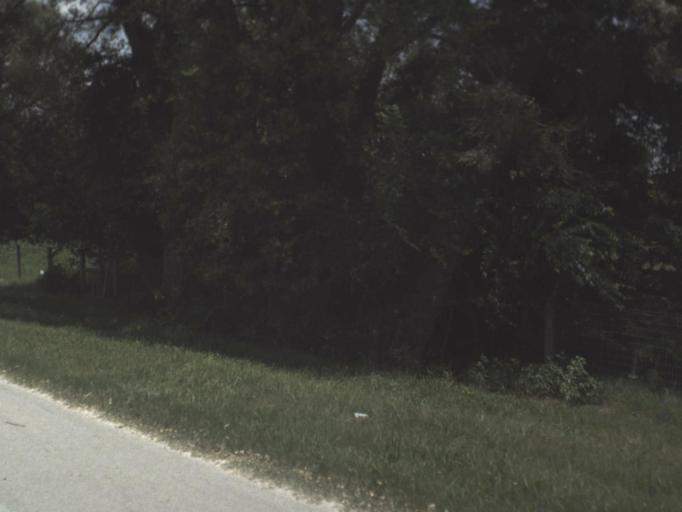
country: US
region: Florida
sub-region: Gilchrist County
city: Trenton
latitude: 29.7231
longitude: -82.8576
